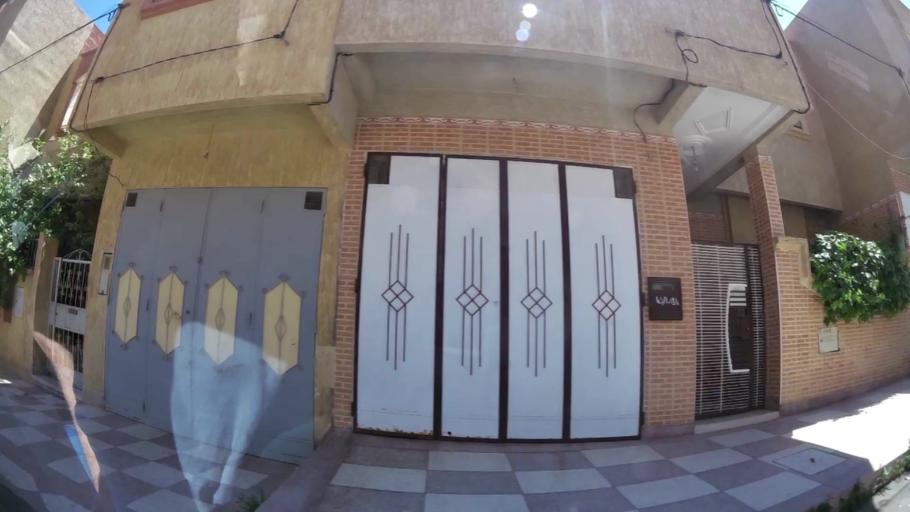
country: MA
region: Oriental
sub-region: Oujda-Angad
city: Oujda
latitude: 34.6779
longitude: -1.9393
